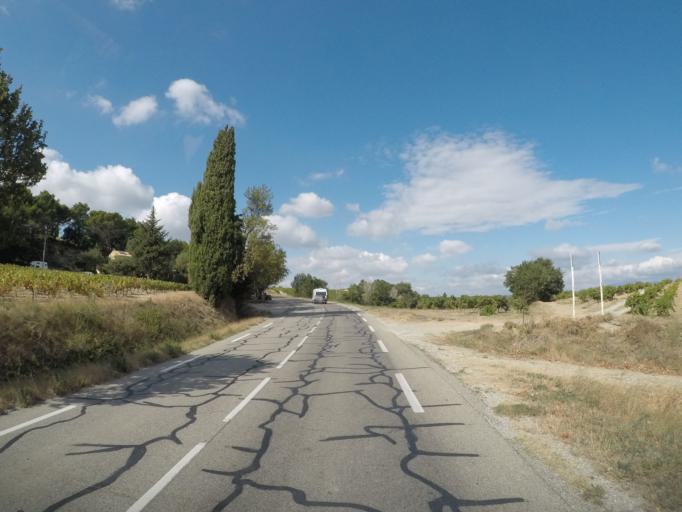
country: FR
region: Provence-Alpes-Cote d'Azur
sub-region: Departement du Vaucluse
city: Vaison-la-Romaine
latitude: 44.2692
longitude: 5.0182
